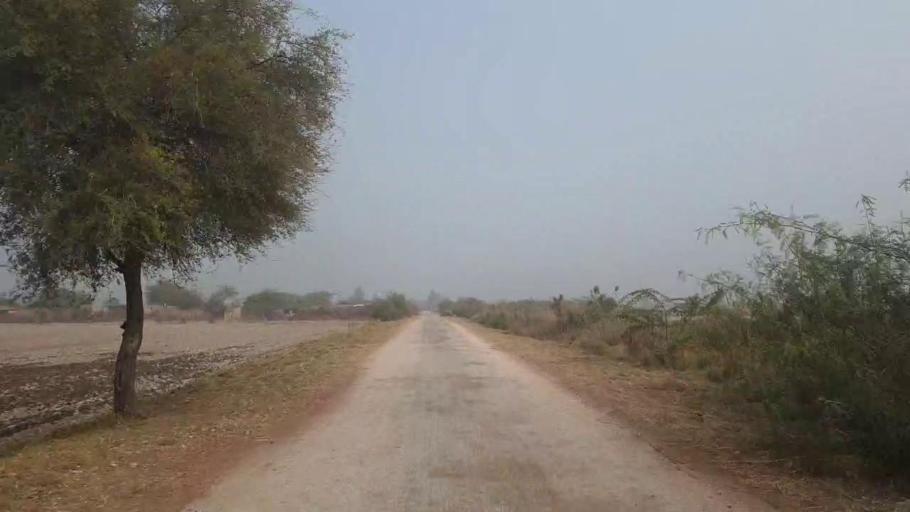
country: PK
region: Sindh
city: Bhit Shah
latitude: 25.8156
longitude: 68.5611
